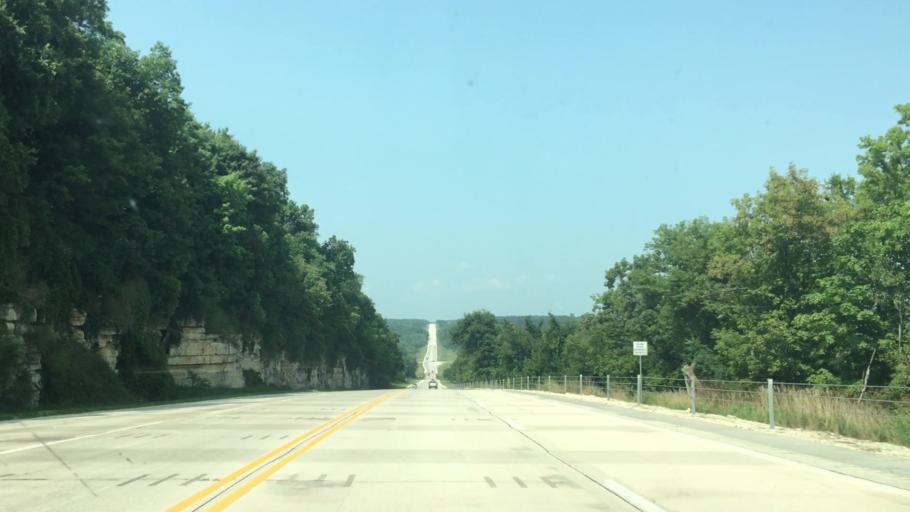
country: US
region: Iowa
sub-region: Winneshiek County
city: Decorah
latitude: 43.3082
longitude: -91.8152
